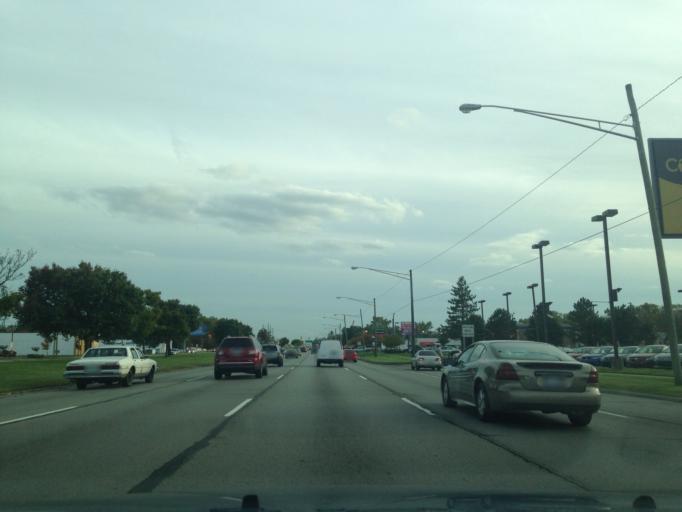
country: US
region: Michigan
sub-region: Wayne County
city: Redford
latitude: 42.3970
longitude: -83.2770
